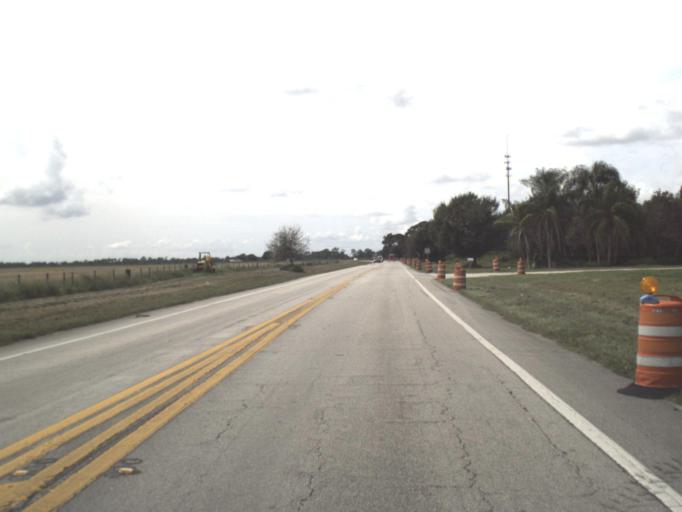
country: US
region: Florida
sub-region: Okeechobee County
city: Taylor Creek
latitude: 27.2899
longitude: -80.6993
